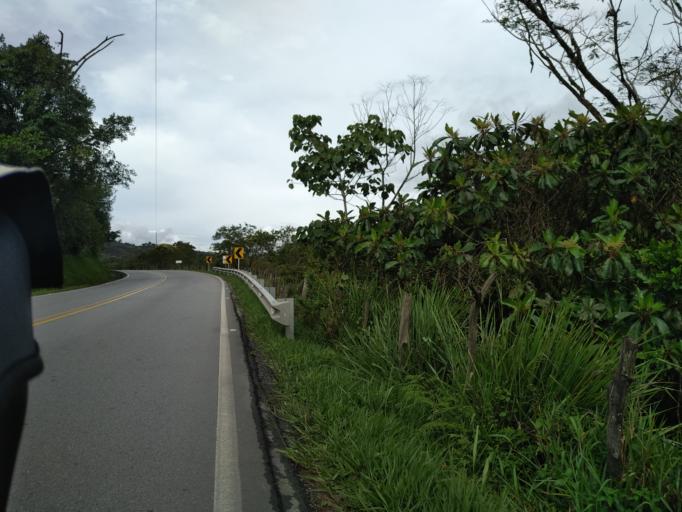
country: CO
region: Santander
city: Suaita
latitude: 6.1048
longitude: -73.3692
